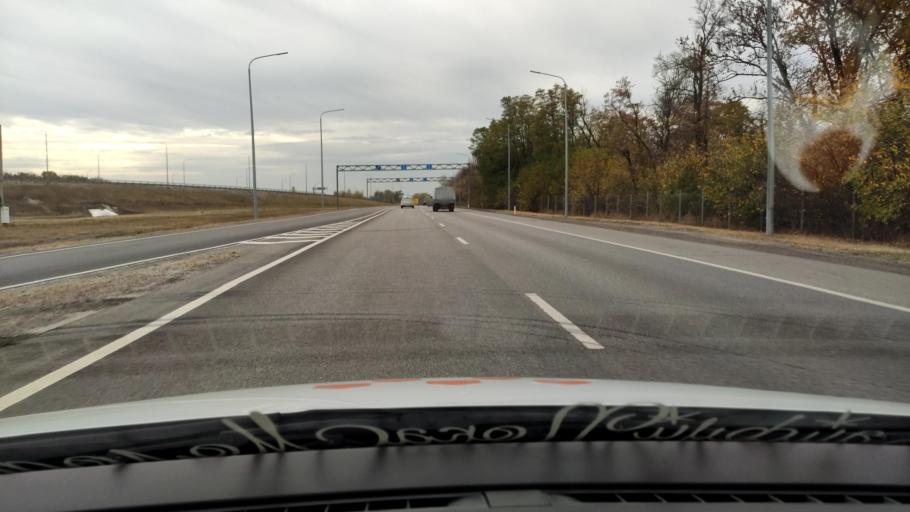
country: RU
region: Voronezj
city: Podgornoye
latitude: 51.8379
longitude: 39.2138
